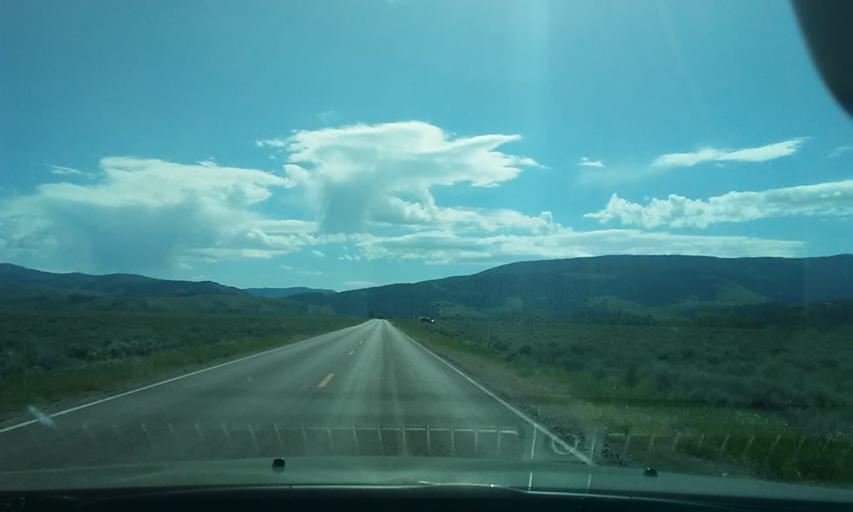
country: US
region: Wyoming
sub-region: Teton County
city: Jackson
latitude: 43.6253
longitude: -110.6565
